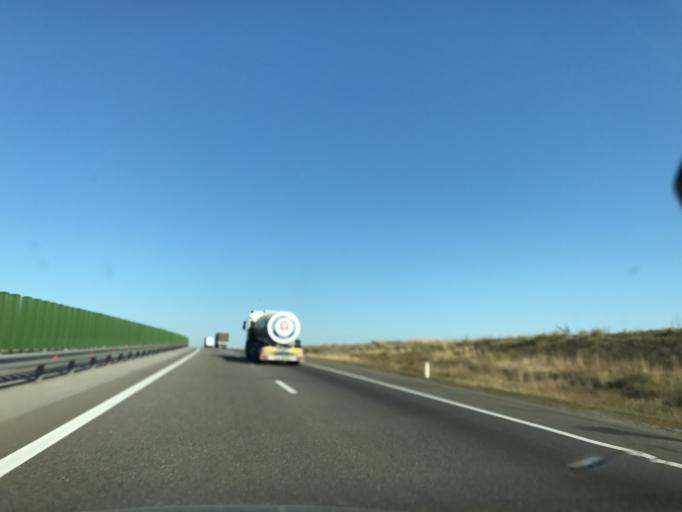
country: RU
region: Rostov
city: Tarasovskiy
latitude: 48.7373
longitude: 40.4003
